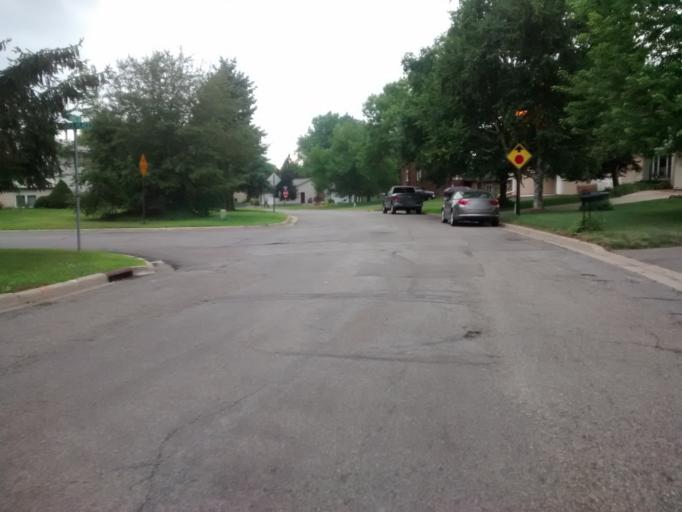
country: US
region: Minnesota
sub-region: Dakota County
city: Burnsville
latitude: 44.7528
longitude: -93.2996
